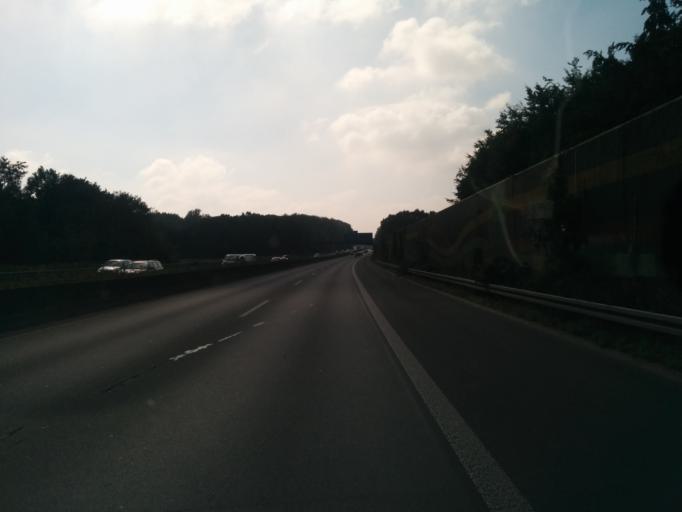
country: DE
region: North Rhine-Westphalia
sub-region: Regierungsbezirk Munster
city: Recklinghausen
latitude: 51.5957
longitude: 7.1863
